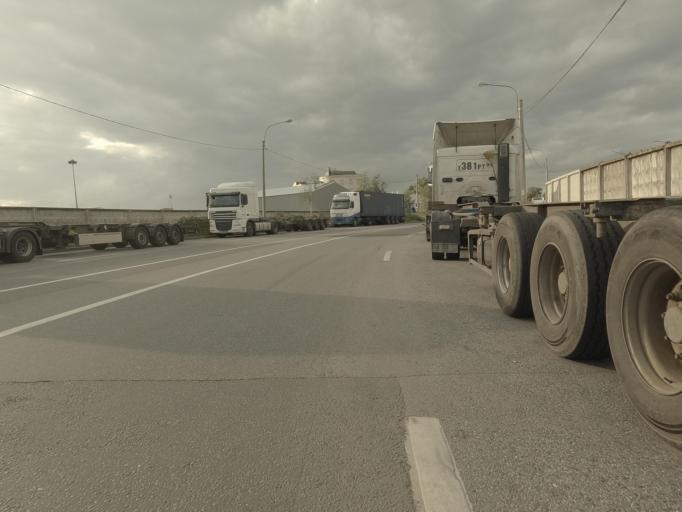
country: RU
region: St.-Petersburg
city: Avtovo
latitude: 59.8665
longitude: 30.2379
